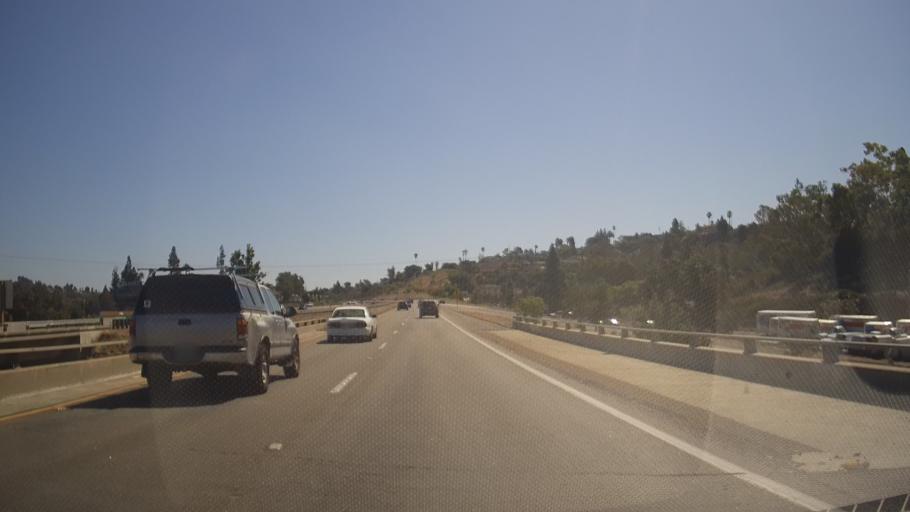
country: US
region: California
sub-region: San Diego County
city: Spring Valley
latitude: 32.7464
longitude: -116.9906
